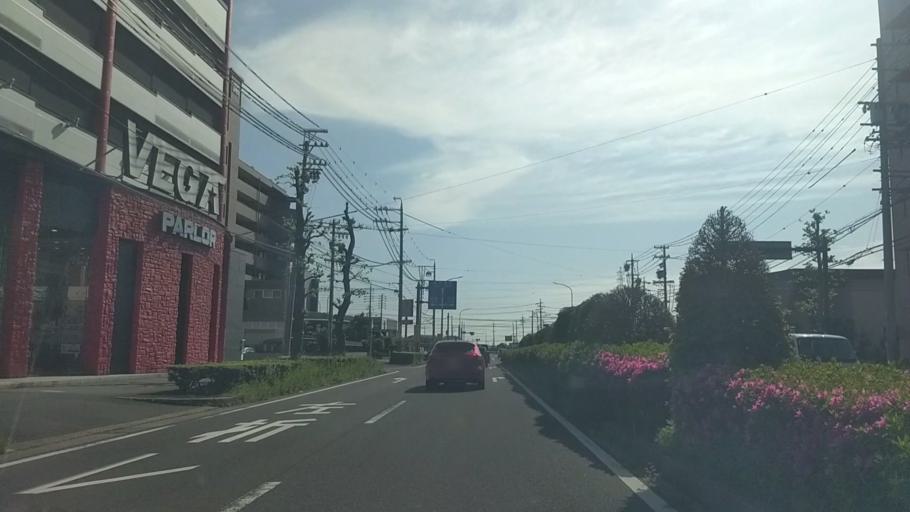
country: JP
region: Aichi
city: Anjo
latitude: 34.9640
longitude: 137.0617
